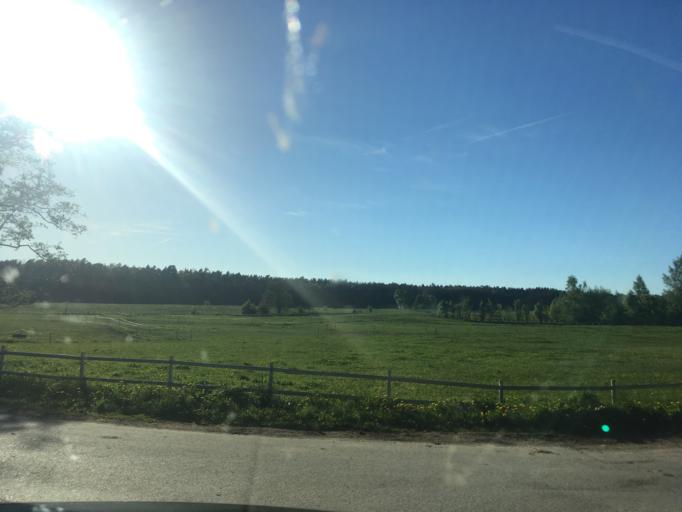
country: PL
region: Warmian-Masurian Voivodeship
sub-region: Powiat piski
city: Ruciane-Nida
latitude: 53.6872
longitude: 21.4690
